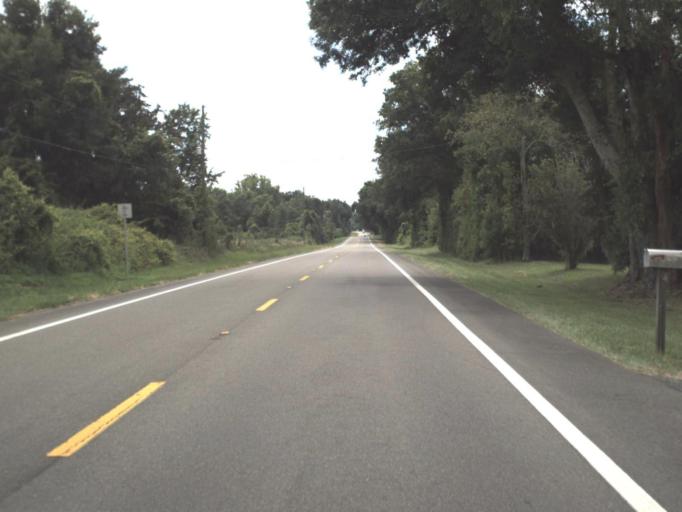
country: US
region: Florida
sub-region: Alachua County
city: Archer
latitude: 29.4970
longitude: -82.4959
